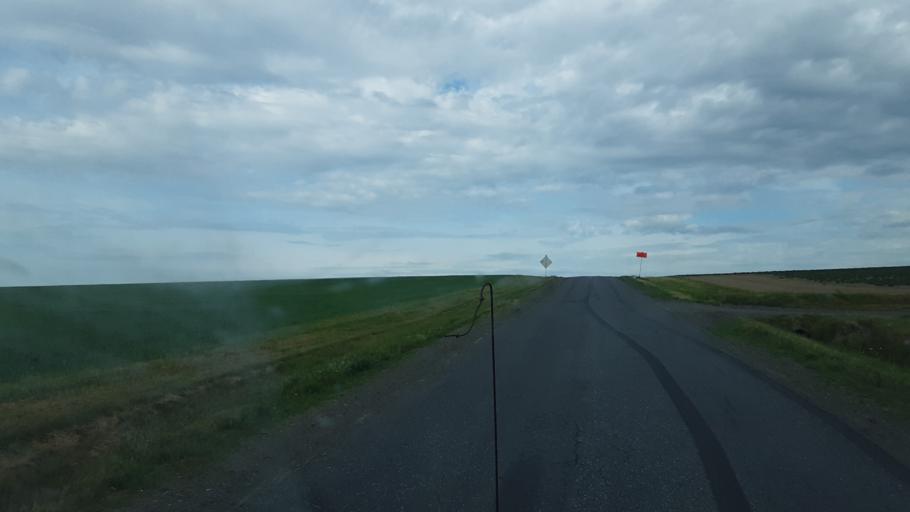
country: US
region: Maine
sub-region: Aroostook County
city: Caribou
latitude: 46.8116
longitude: -67.9977
